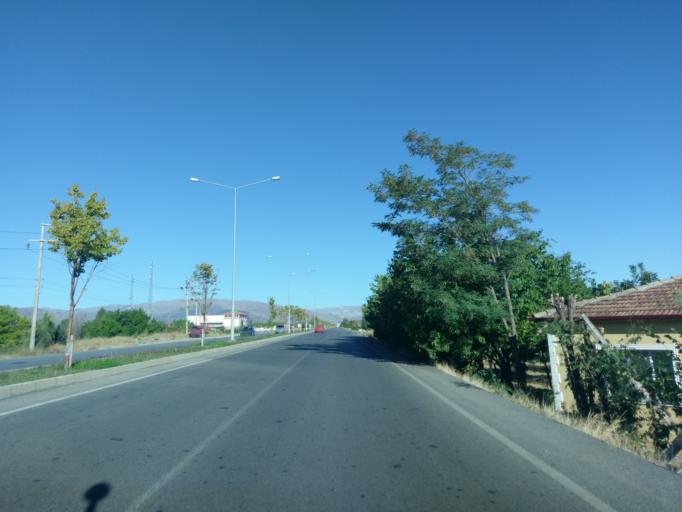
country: TR
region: Erzincan
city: Erzincan
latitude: 39.7751
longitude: 39.4184
